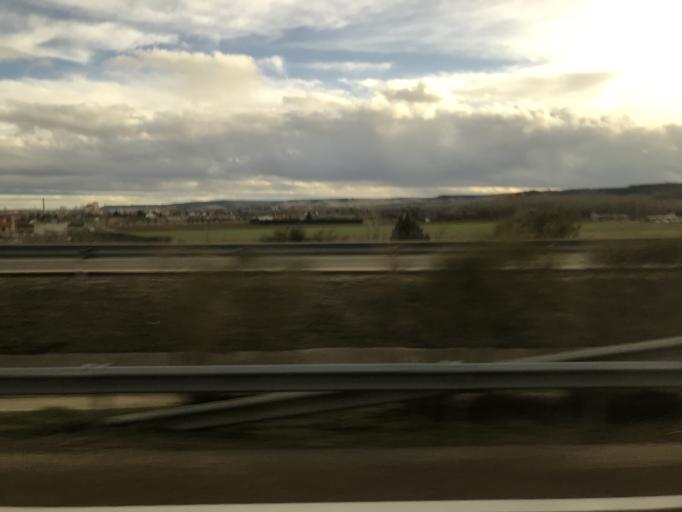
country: ES
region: Castille and Leon
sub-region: Provincia de Palencia
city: Grijota
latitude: 42.0409
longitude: -4.5502
